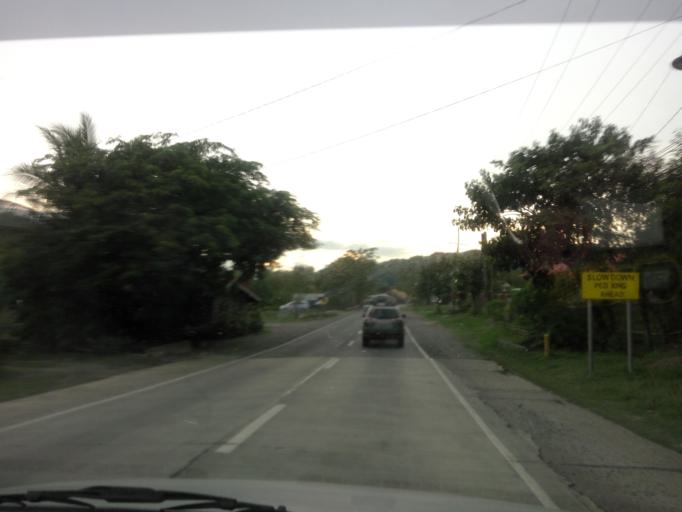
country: PH
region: Ilocos
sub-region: Province of La Union
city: Damortis
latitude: 16.2344
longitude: 120.4337
